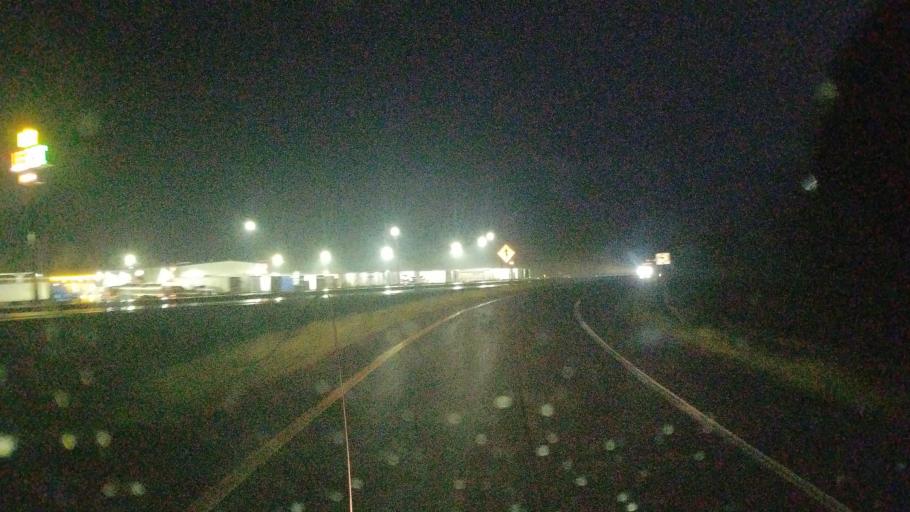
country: US
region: Michigan
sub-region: Washtenaw County
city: Milan
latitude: 42.0776
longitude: -83.6715
